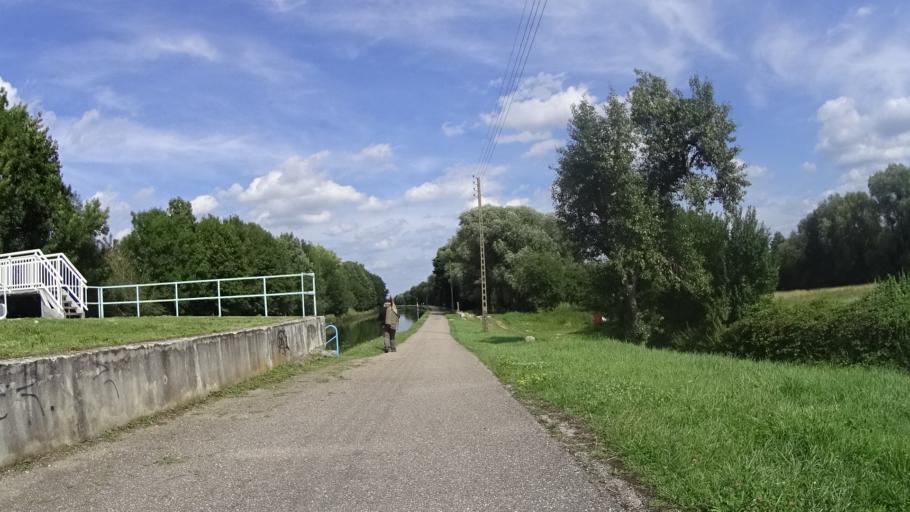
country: FR
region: Lorraine
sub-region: Departement de Meurthe-et-Moselle
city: Ecrouves
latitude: 48.6771
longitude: 5.8724
